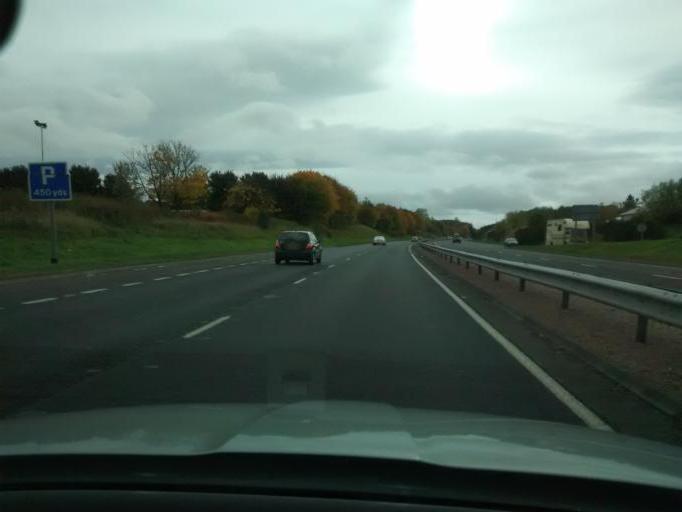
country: GB
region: Scotland
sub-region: Perth and Kinross
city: Luncarty
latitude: 56.4065
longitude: -3.4831
